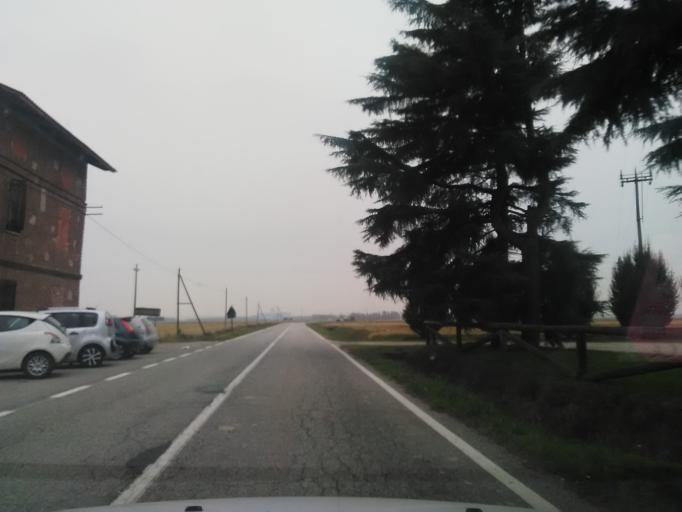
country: IT
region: Piedmont
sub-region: Provincia di Vercelli
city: Fontanetto Po
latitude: 45.2548
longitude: 8.1676
